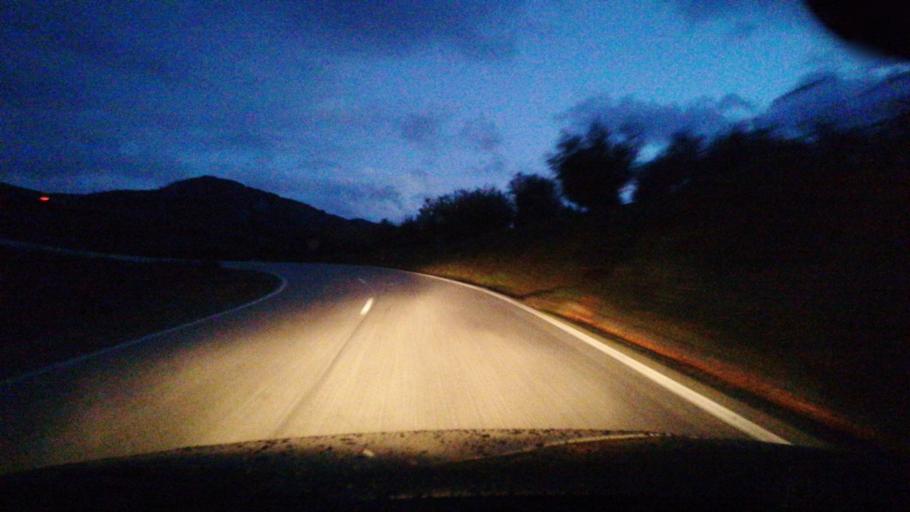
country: PT
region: Viseu
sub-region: Tabuaco
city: Tabuaco
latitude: 41.1437
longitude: -7.5371
